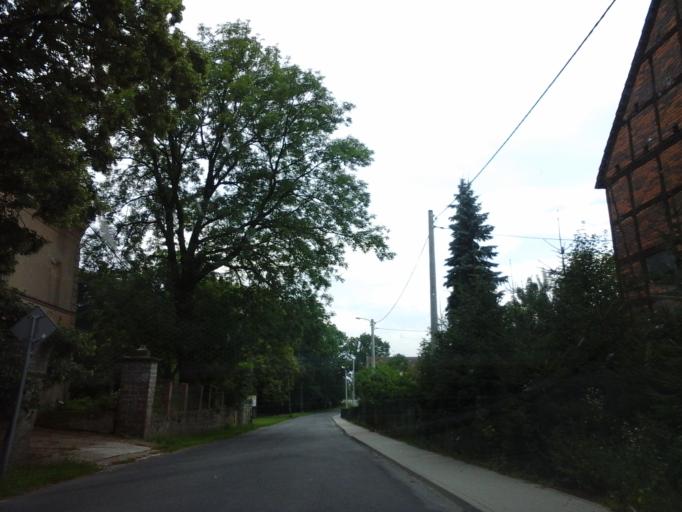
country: PL
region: Lower Silesian Voivodeship
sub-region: Powiat zabkowicki
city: Zabkowice Slaskie
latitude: 50.6182
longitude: 16.8486
